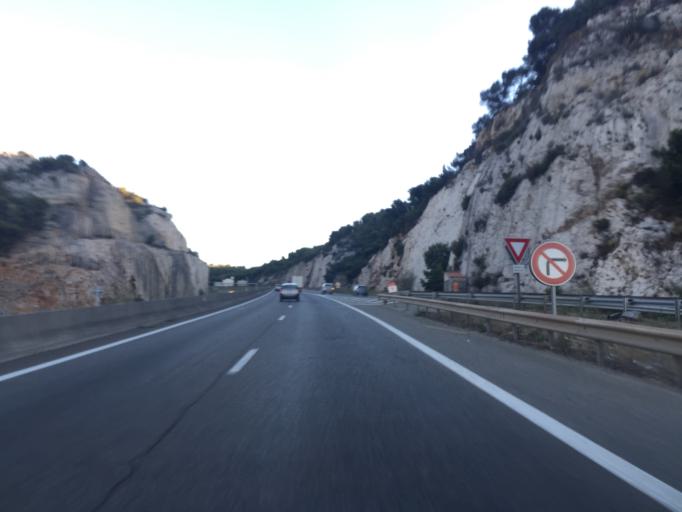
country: FR
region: Provence-Alpes-Cote d'Azur
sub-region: Departement des Bouches-du-Rhone
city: Les Pennes-Mirabeau
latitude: 43.3974
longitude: 5.2982
